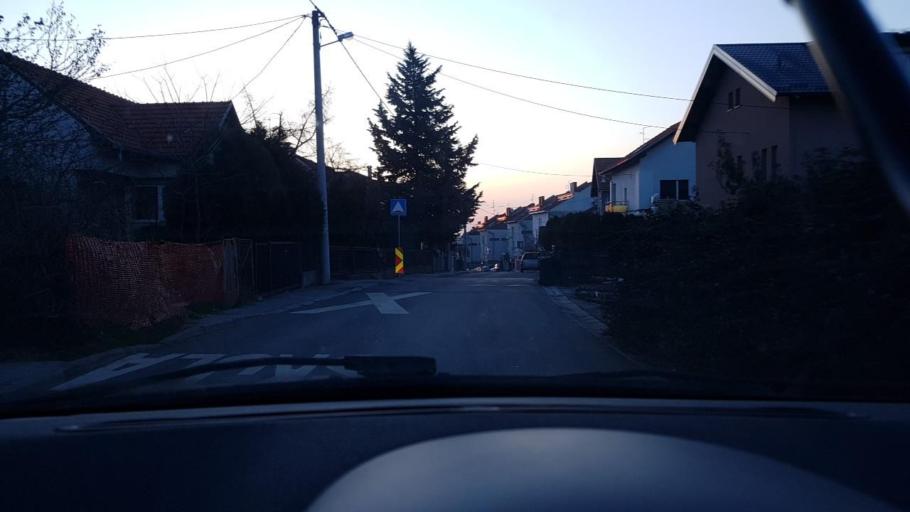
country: HR
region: Grad Zagreb
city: Zagreb
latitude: 45.8320
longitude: 16.0009
